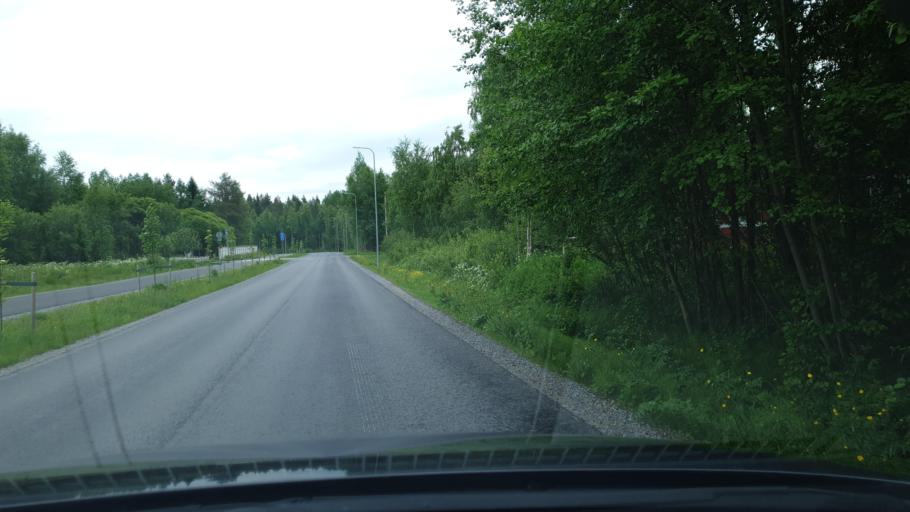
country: FI
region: Northern Ostrobothnia
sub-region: Oulunkaari
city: Ii
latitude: 65.3087
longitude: 25.3814
